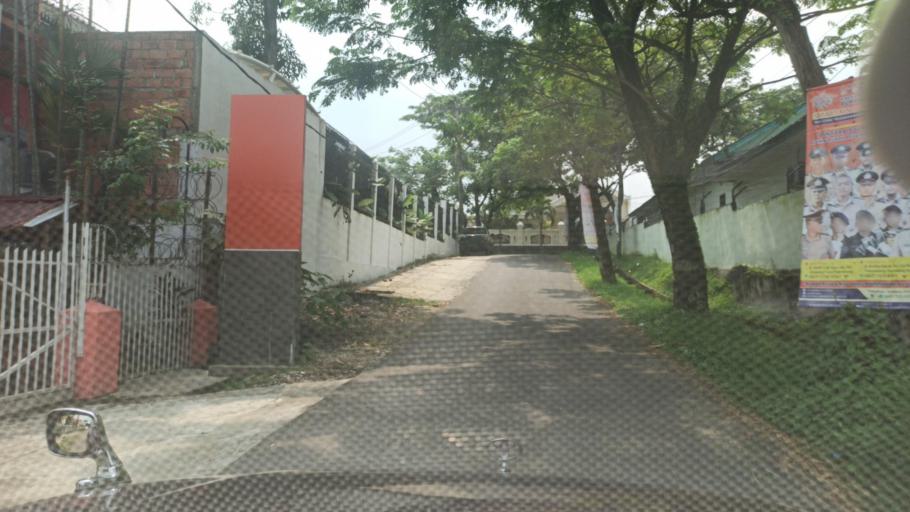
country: ID
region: South Sumatra
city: Plaju
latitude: -2.9885
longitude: 104.7409
